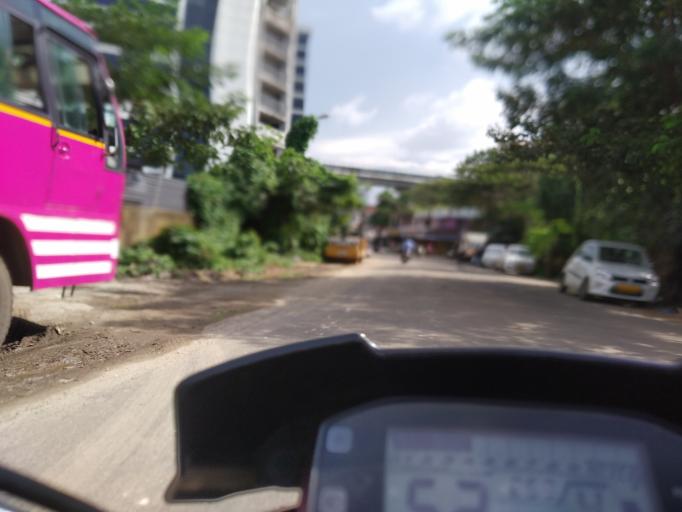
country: IN
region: Kerala
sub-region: Ernakulam
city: Cochin
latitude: 9.9933
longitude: 76.2892
